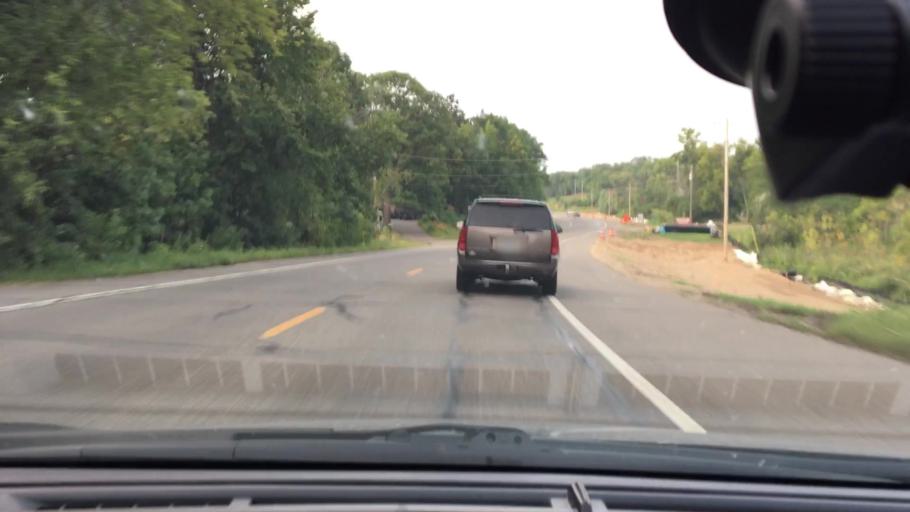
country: US
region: Minnesota
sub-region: Crow Wing County
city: Crosby
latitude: 46.4780
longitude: -93.9009
